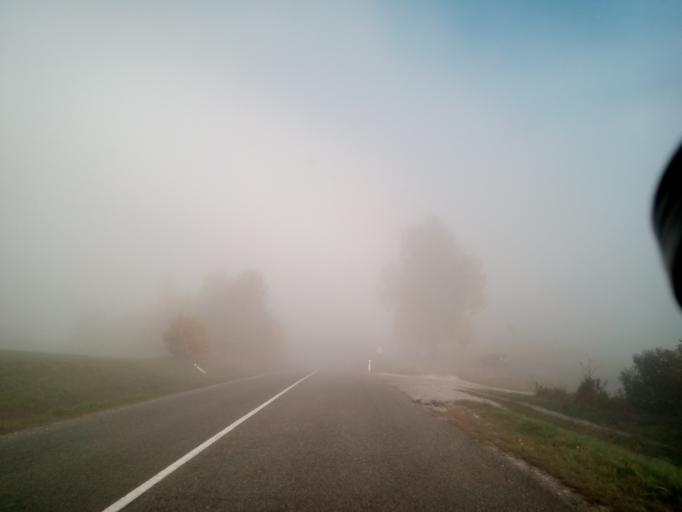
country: SK
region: Kosicky
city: Gelnica
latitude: 48.8489
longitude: 21.0321
